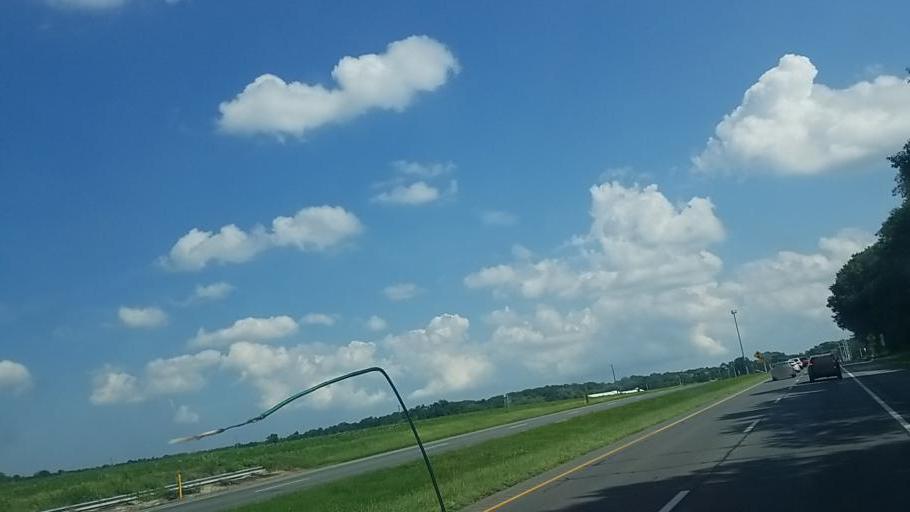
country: US
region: Delaware
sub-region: Sussex County
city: Millsboro
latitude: 38.6024
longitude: -75.3206
